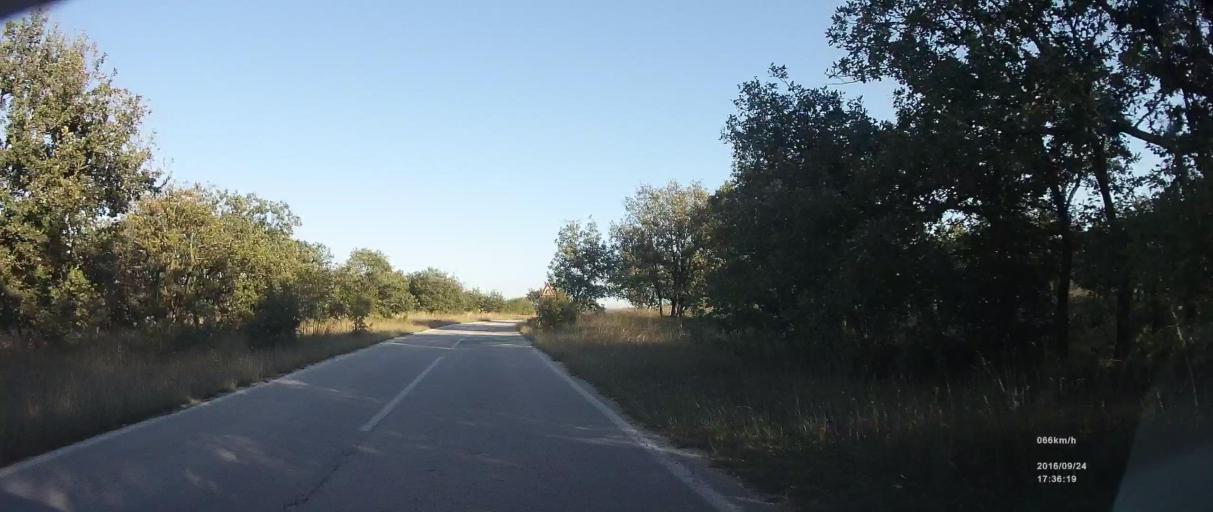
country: HR
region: Zadarska
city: Posedarje
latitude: 44.1556
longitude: 15.4746
